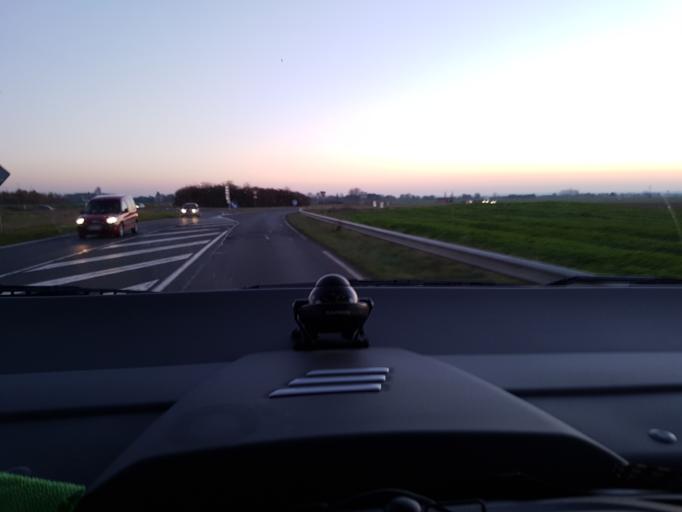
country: FR
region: Picardie
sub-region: Departement de la Somme
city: Nouvion
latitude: 50.2579
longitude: 1.7447
